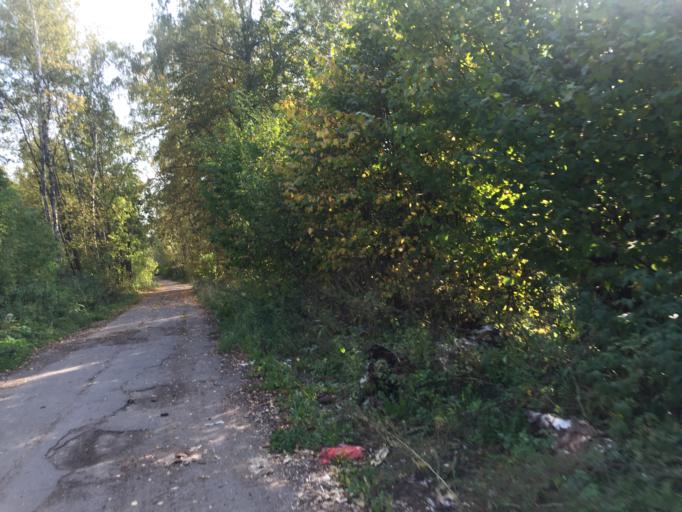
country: RU
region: Moscow
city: Babushkin
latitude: 55.8495
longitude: 37.7194
